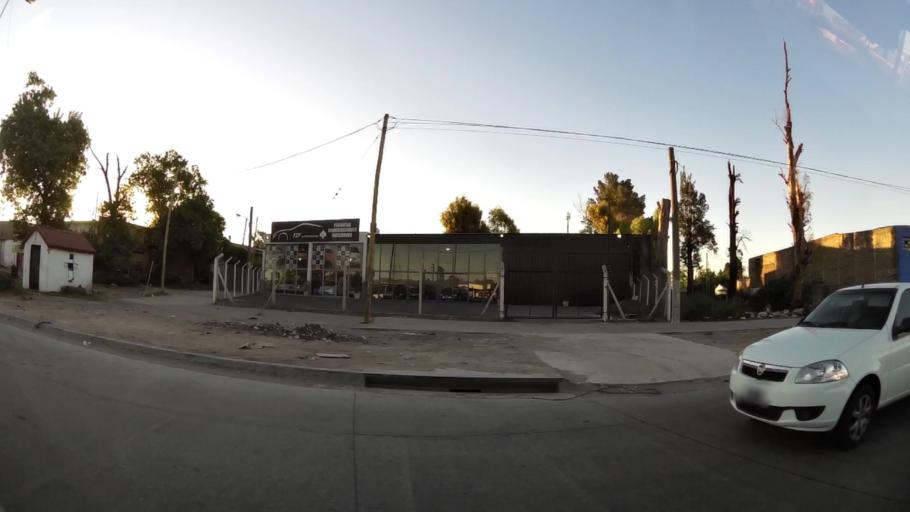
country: AR
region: Buenos Aires
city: Pontevedra
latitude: -34.7528
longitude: -58.6140
